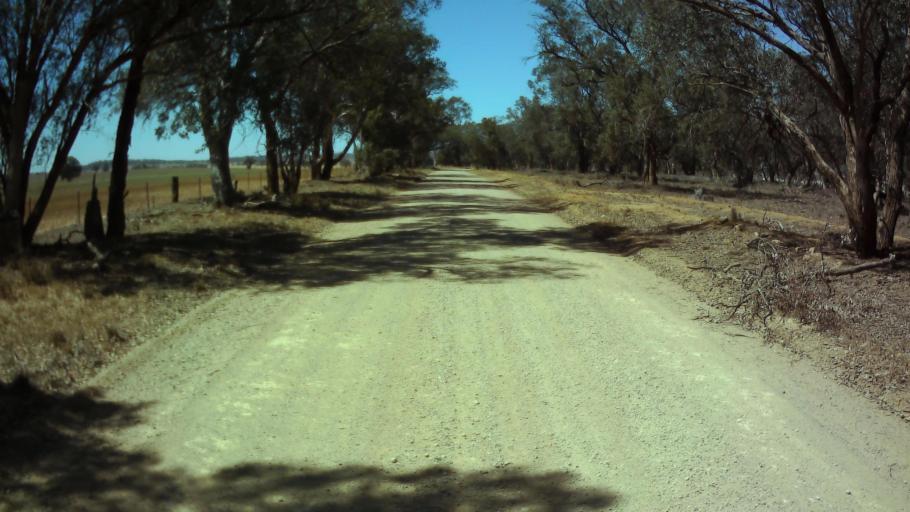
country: AU
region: New South Wales
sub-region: Weddin
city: Grenfell
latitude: -33.8758
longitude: 148.0888
